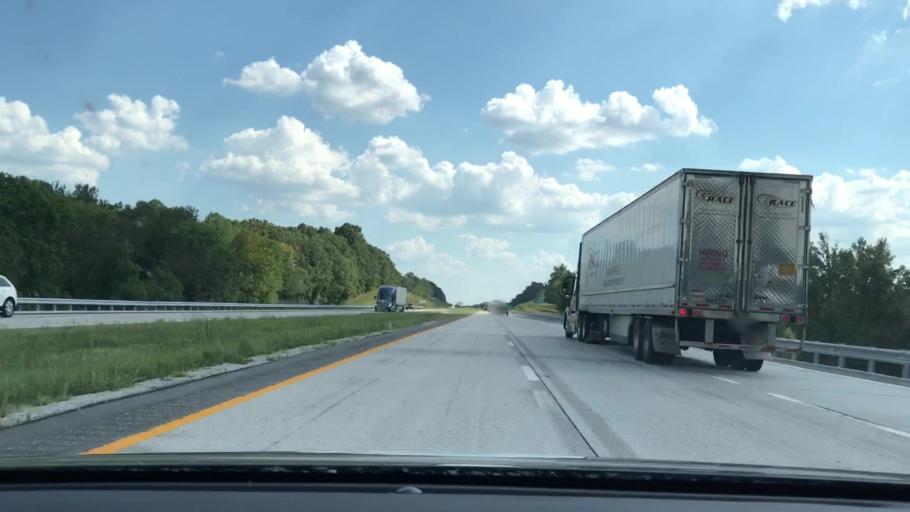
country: US
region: Kentucky
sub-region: Ohio County
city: Oak Grove
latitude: 37.3789
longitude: -86.8059
